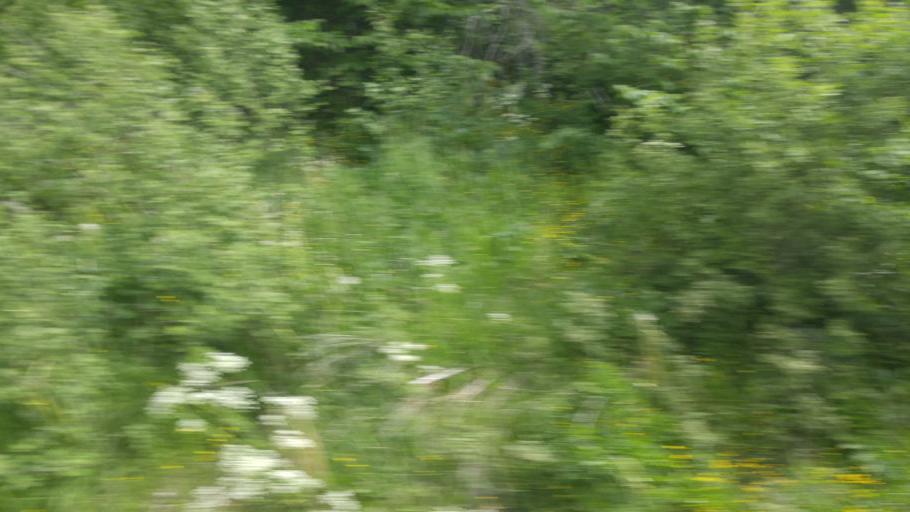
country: NO
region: Sor-Trondelag
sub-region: Melhus
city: Lundamo
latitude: 63.2179
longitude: 10.3080
